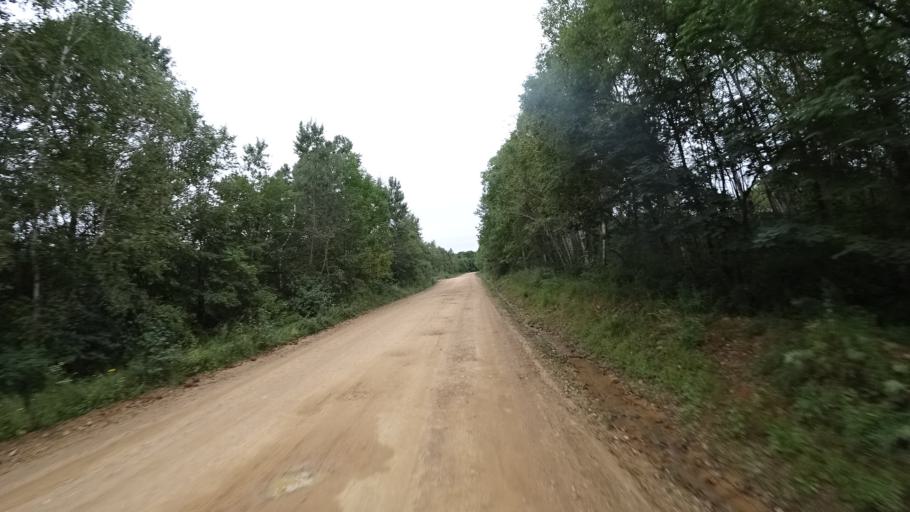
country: RU
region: Primorskiy
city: Rettikhovka
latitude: 44.1806
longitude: 132.8042
